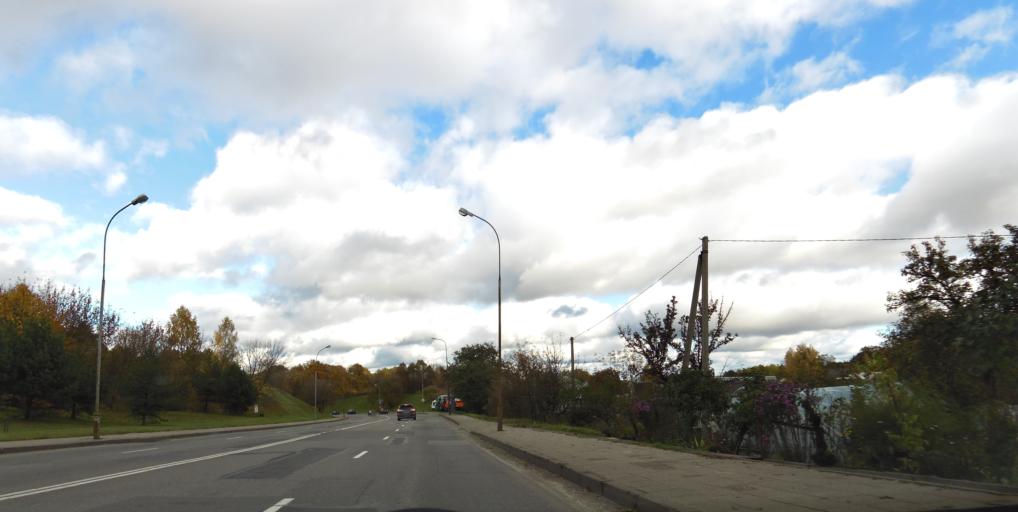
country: LT
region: Vilnius County
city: Rasos
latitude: 54.6642
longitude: 25.3041
